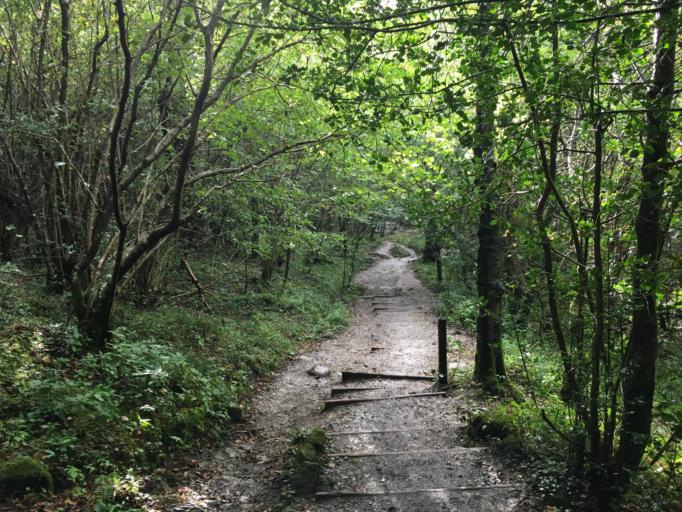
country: GB
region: England
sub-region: North Yorkshire
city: Sleights
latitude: 54.3990
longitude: -0.7309
